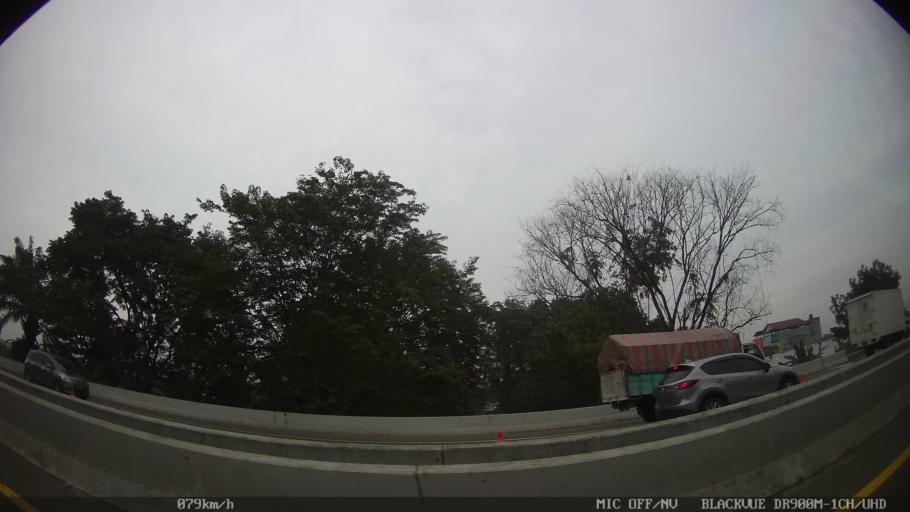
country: ID
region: North Sumatra
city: Medan
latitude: 3.5836
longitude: 98.7241
